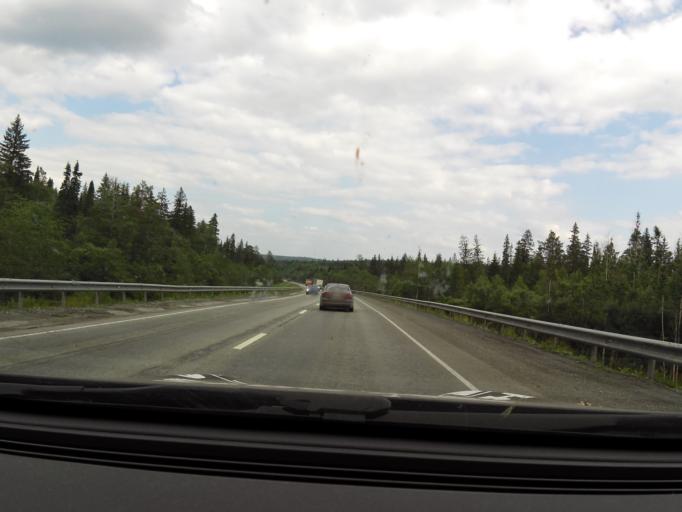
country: RU
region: Sverdlovsk
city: Bilimbay
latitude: 56.8535
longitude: 59.7760
